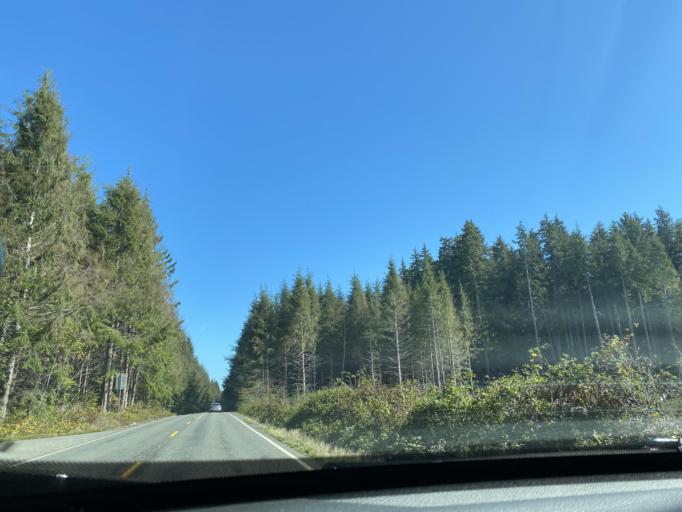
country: US
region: Washington
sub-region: Clallam County
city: Forks
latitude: 47.9189
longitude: -124.5184
